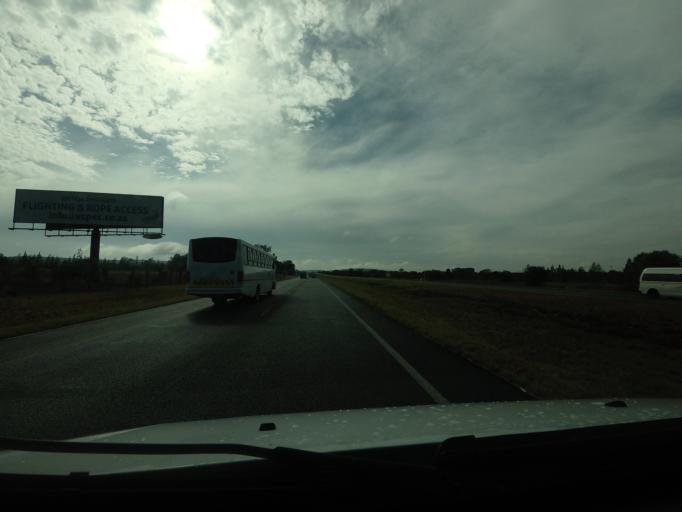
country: ZA
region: Gauteng
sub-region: City of Tshwane Metropolitan Municipality
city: Cullinan
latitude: -25.7708
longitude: 28.4177
